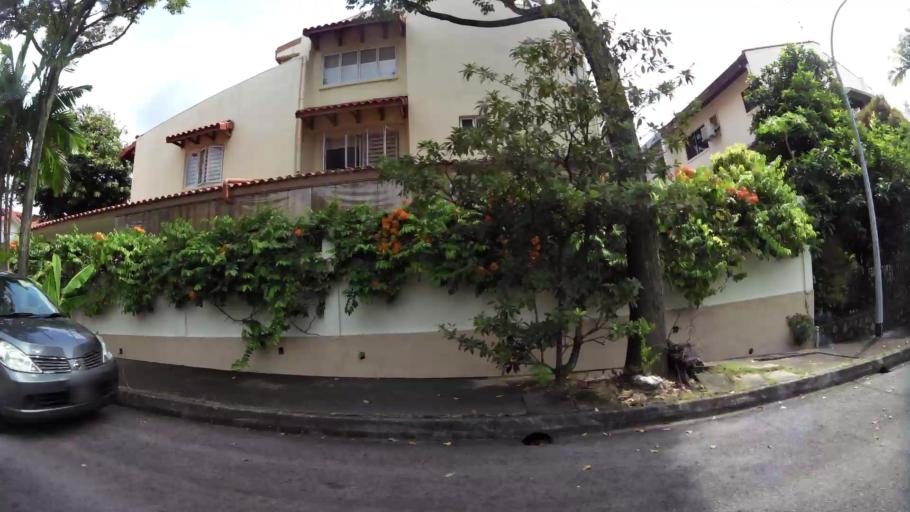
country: SG
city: Singapore
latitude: 1.3387
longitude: 103.7648
